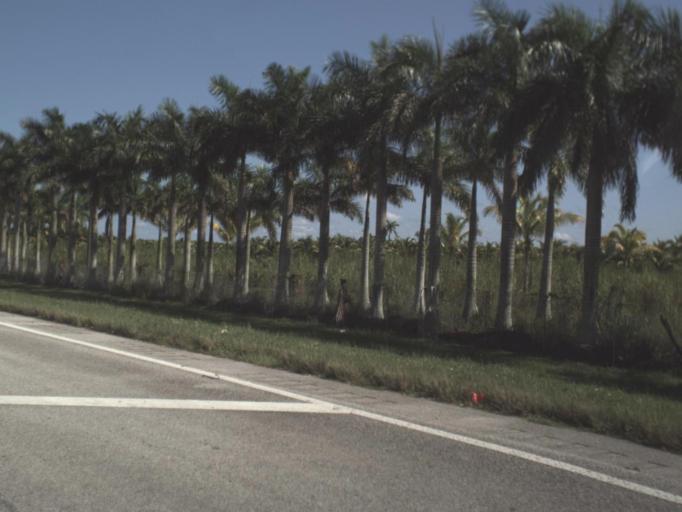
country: US
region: Florida
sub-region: Miami-Dade County
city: Goulds
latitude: 25.5399
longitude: -80.3640
